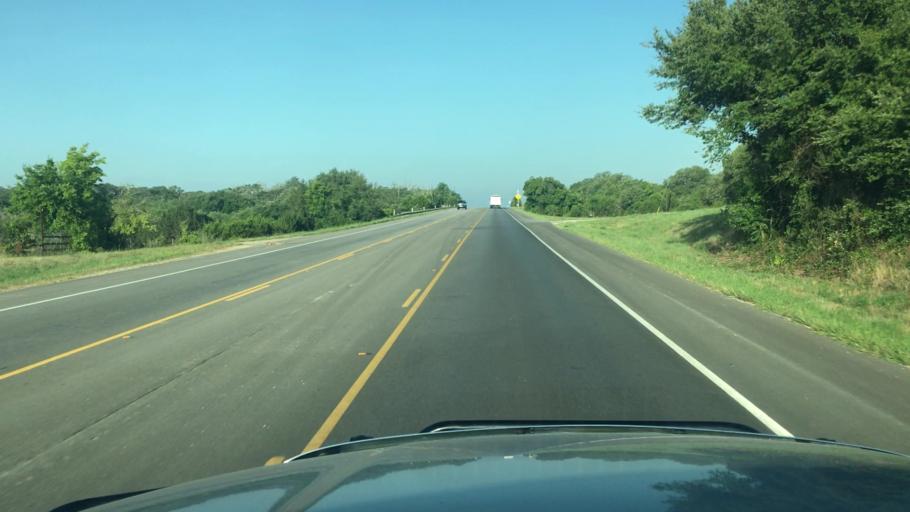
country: US
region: Texas
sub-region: Hays County
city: Dripping Springs
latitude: 30.2009
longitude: -98.1559
